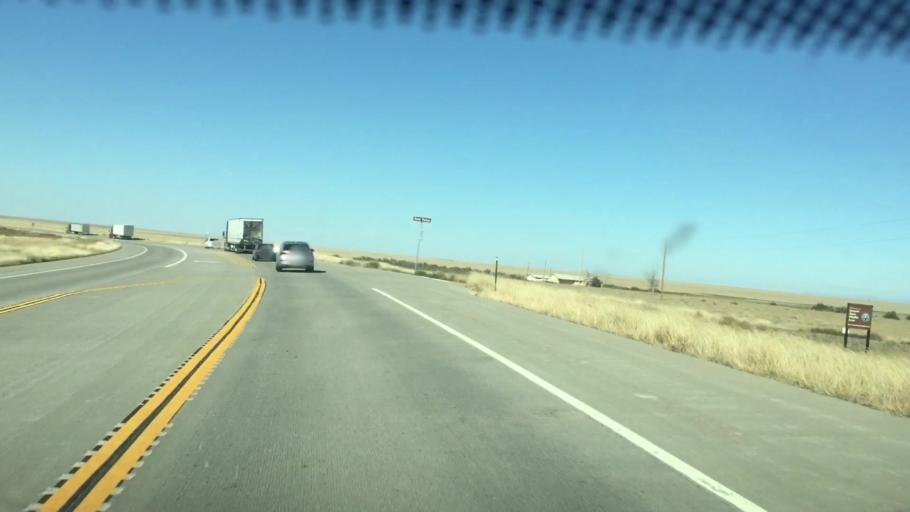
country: US
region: Colorado
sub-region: Kiowa County
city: Eads
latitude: 38.3475
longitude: -102.7145
